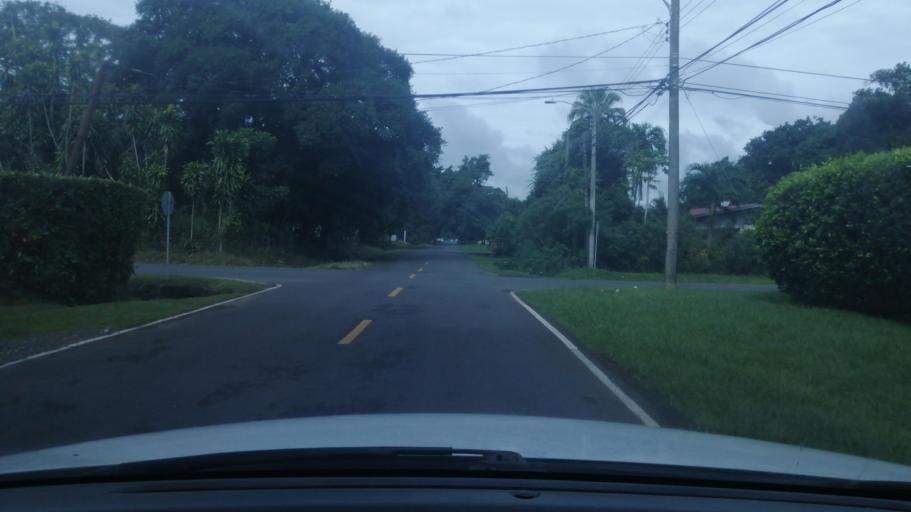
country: PA
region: Chiriqui
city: David
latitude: 8.4380
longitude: -82.4284
